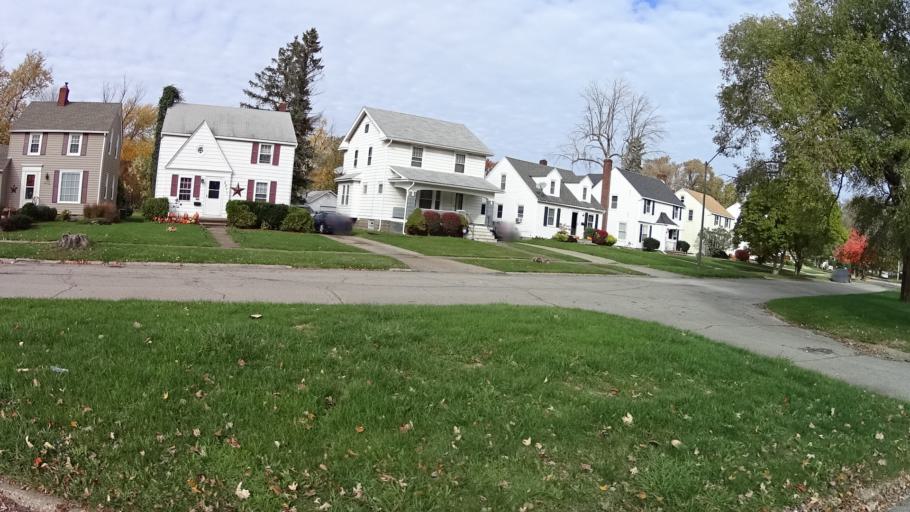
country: US
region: Ohio
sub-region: Lorain County
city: Sheffield Lake
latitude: 41.4782
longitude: -82.1409
